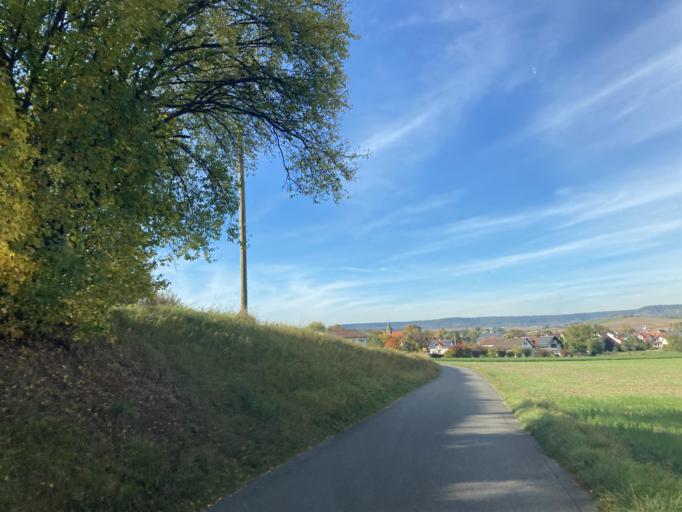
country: DE
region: Baden-Wuerttemberg
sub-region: Tuebingen Region
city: Rottenburg
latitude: 48.5215
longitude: 8.9642
